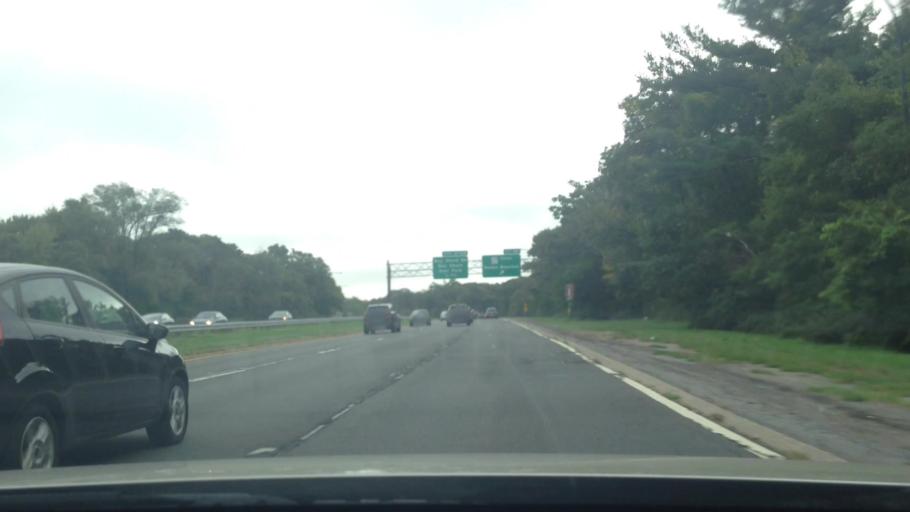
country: US
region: New York
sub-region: Suffolk County
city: Bay Wood
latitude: 40.7340
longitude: -73.2936
